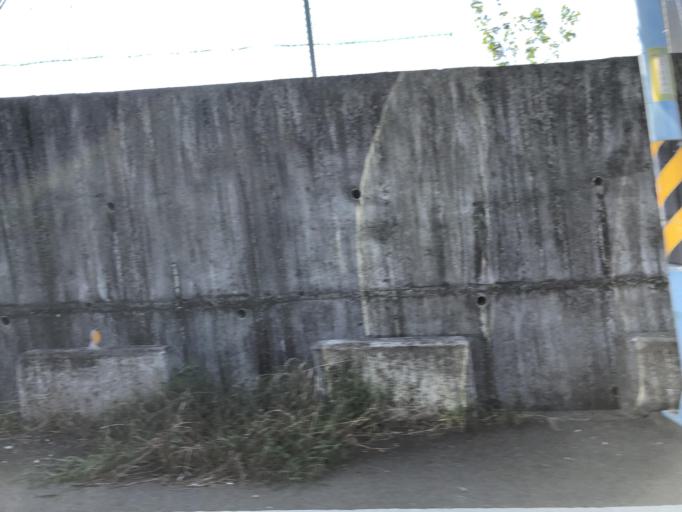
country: TW
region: Taiwan
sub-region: Tainan
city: Tainan
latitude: 23.0349
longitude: 120.3443
